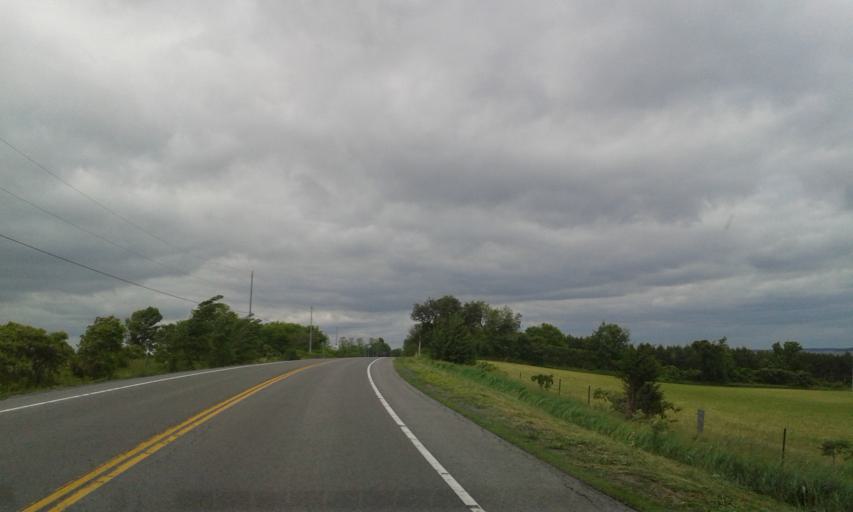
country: CA
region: Ontario
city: Deseronto
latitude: 44.0946
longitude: -76.9471
